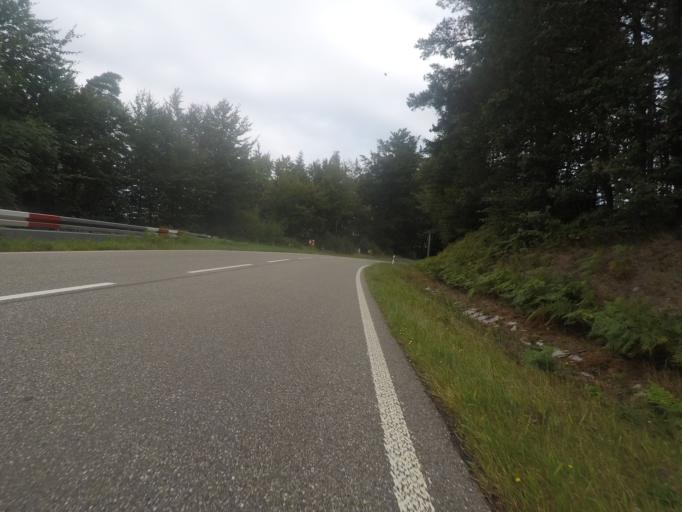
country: DE
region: Baden-Wuerttemberg
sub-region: Karlsruhe Region
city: Gaggenau
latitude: 48.8374
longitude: 8.3723
